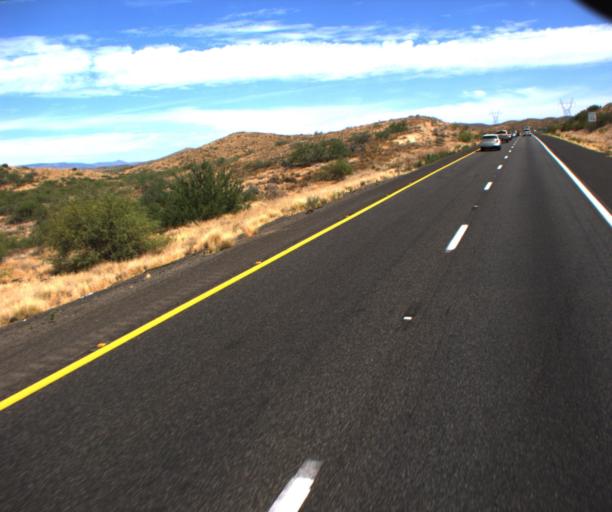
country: US
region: Arizona
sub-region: Yavapai County
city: Cordes Lakes
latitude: 34.2466
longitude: -112.1121
